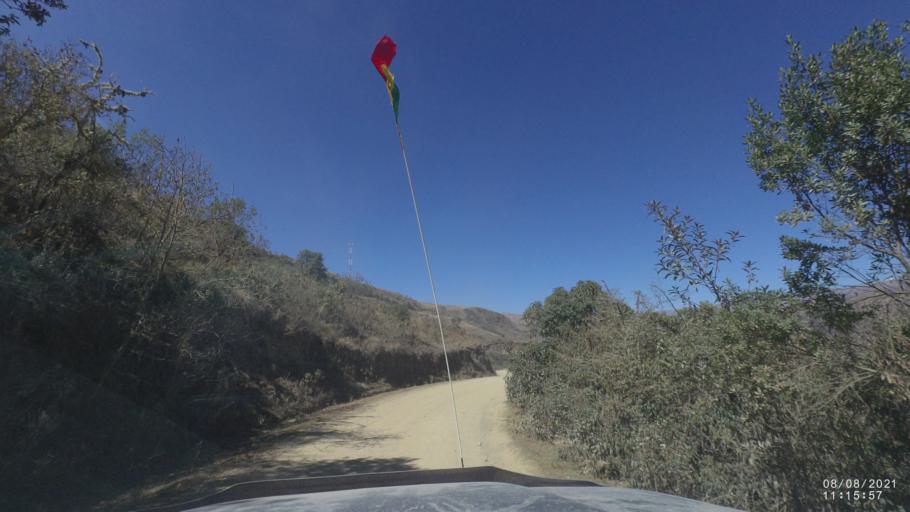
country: BO
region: Cochabamba
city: Colchani
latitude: -16.7775
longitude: -66.6663
